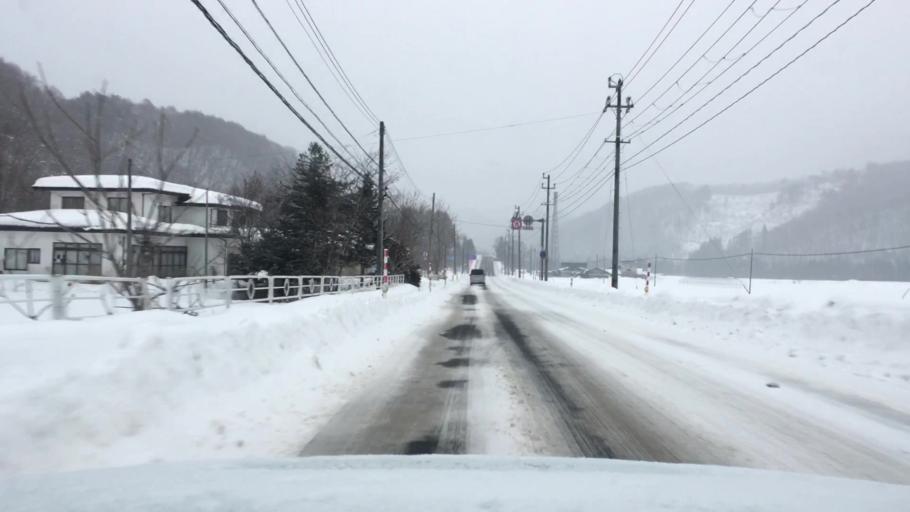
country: JP
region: Akita
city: Hanawa
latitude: 40.0583
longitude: 141.0113
